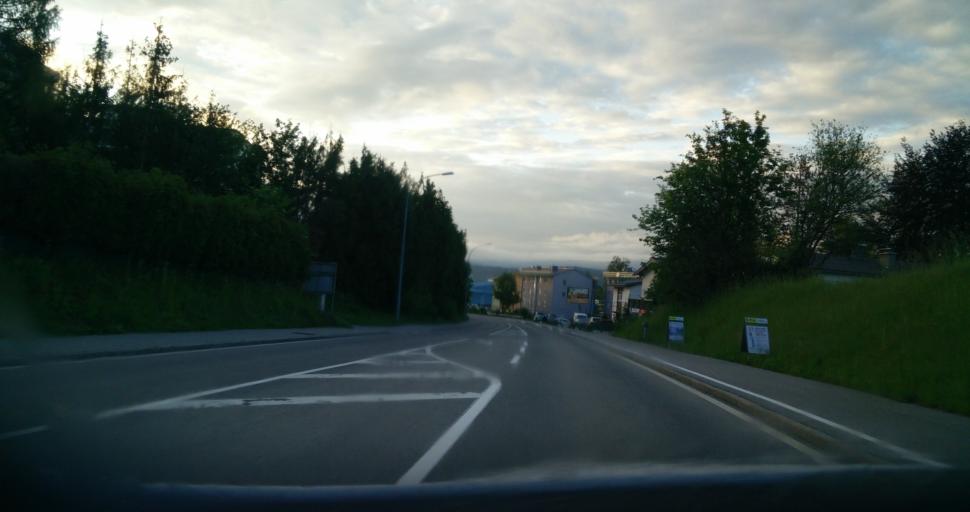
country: AT
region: Carinthia
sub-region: Villach Stadt
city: Villach
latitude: 46.6153
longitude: 13.8265
